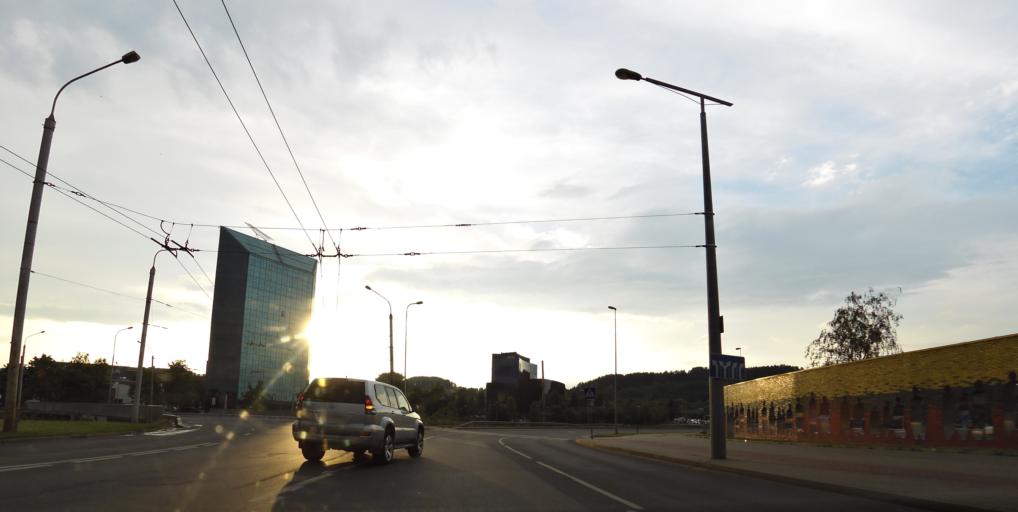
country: LT
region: Vilnius County
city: Seskine
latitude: 54.6989
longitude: 25.2646
